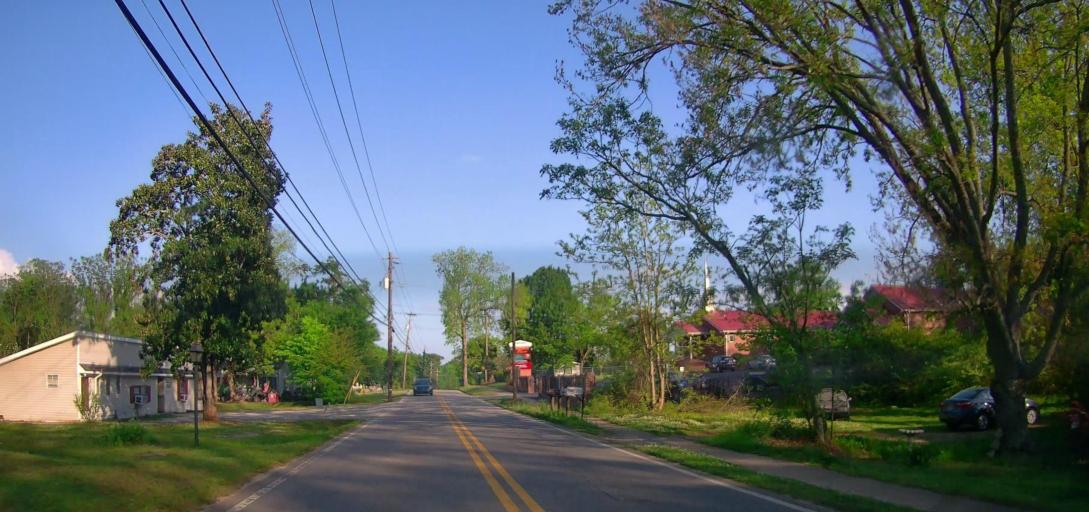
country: US
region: Georgia
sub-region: Putnam County
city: Eatonton
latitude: 33.3230
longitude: -83.3801
